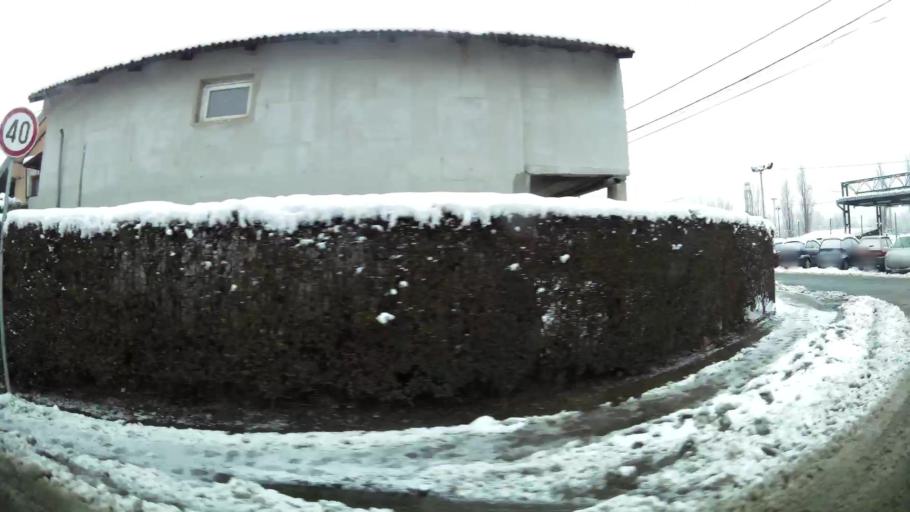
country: RS
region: Central Serbia
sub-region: Belgrade
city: Novi Beograd
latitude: 44.8104
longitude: 20.4433
